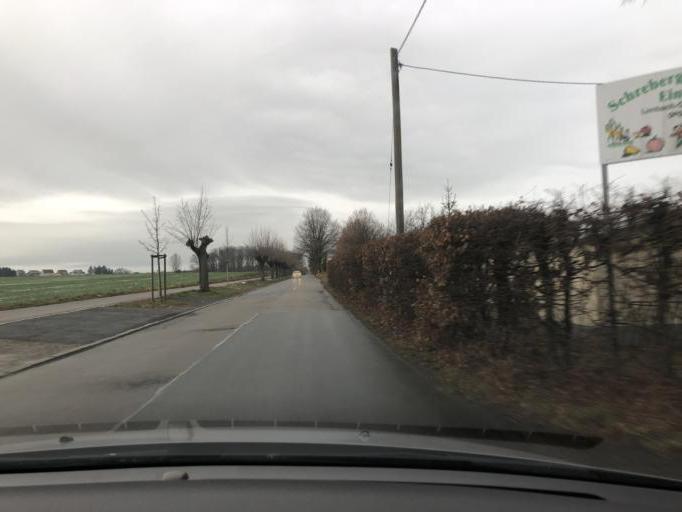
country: DE
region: Saxony
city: Limbach-Oberfrohna
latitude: 50.8602
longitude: 12.7310
